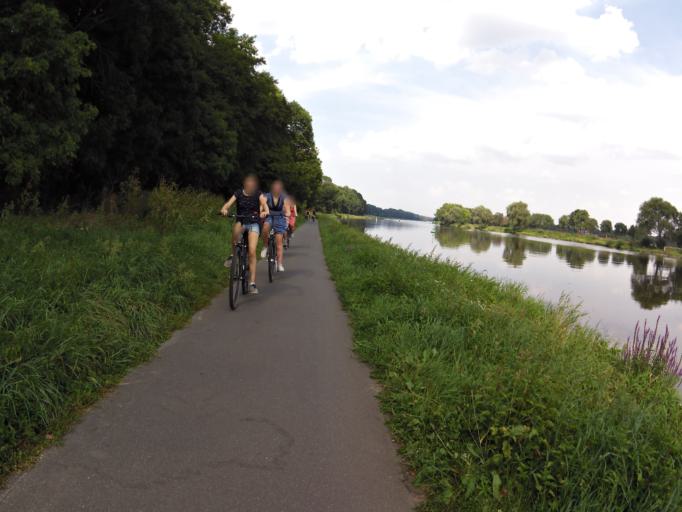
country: DE
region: North Rhine-Westphalia
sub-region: Regierungsbezirk Detmold
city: Minden
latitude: 52.3191
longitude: 8.9219
